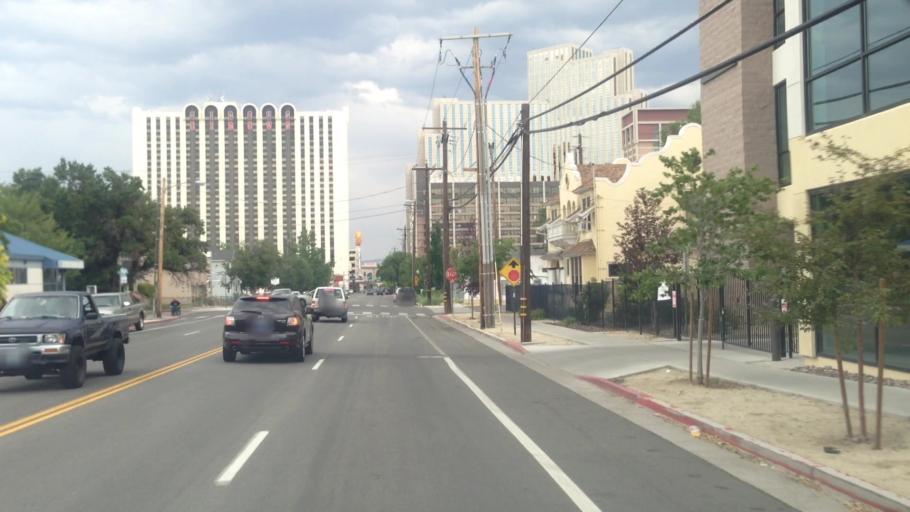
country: US
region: Nevada
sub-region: Washoe County
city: Reno
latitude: 39.5298
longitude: -119.8221
